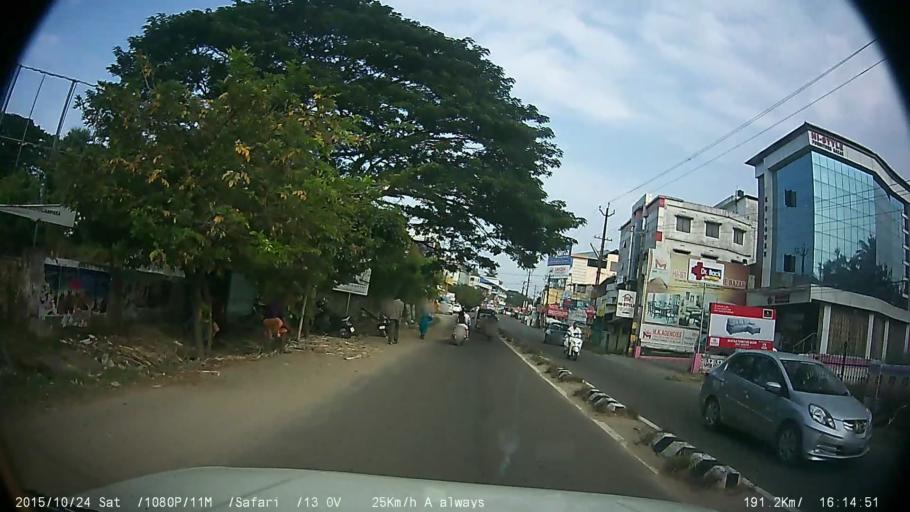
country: IN
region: Kerala
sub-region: Palakkad district
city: Palakkad
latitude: 10.7733
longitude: 76.6647
